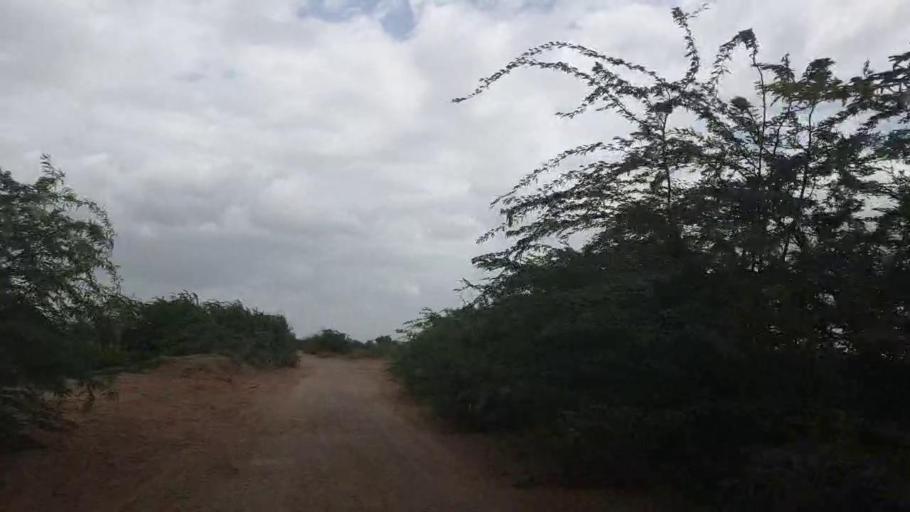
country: PK
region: Sindh
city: Badin
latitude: 24.6437
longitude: 68.9465
